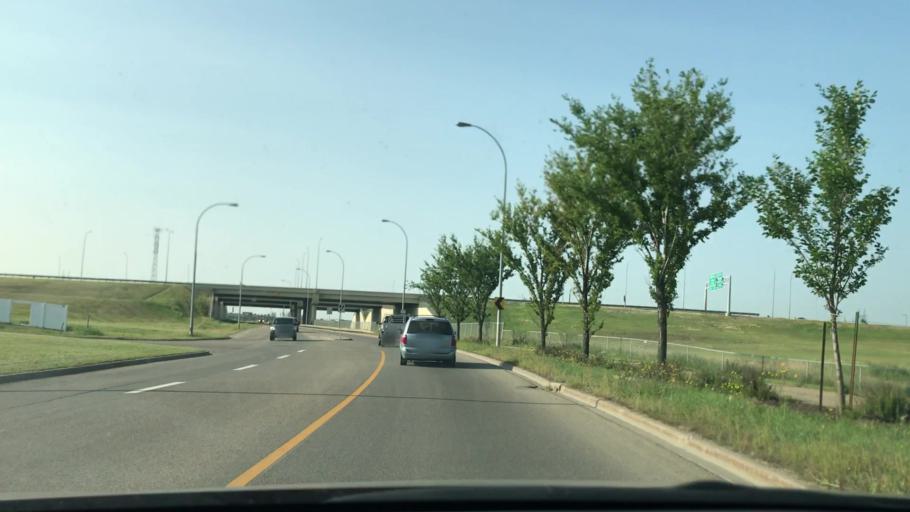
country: CA
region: Alberta
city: Edmonton
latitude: 53.4401
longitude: -113.4845
